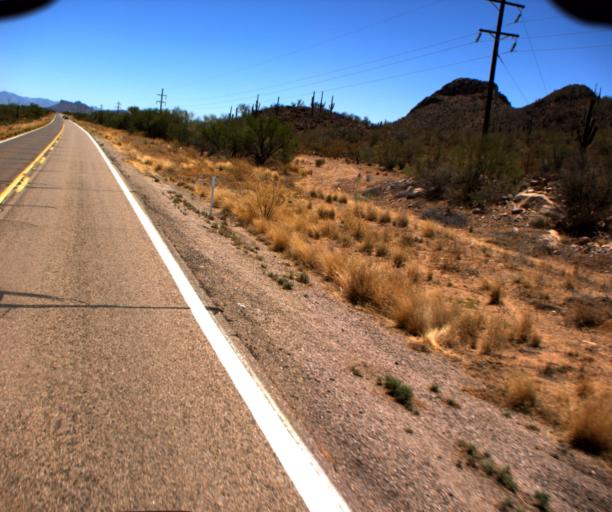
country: US
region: Arizona
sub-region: Pima County
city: Sells
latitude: 31.9554
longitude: -111.9441
